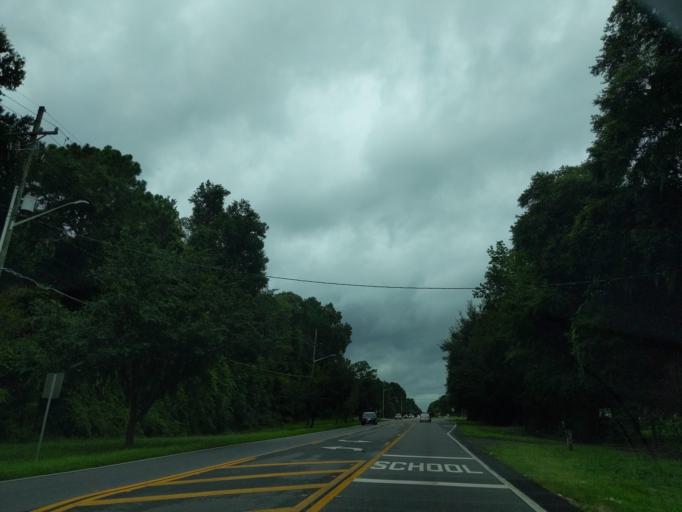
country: US
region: Florida
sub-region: Alachua County
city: Gainesville
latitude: 29.6048
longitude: -82.4226
